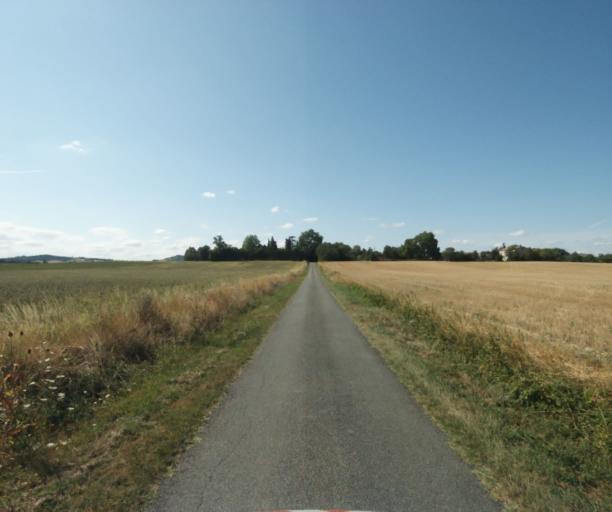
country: FR
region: Midi-Pyrenees
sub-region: Departement de la Haute-Garonne
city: Revel
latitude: 43.4980
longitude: 1.9823
